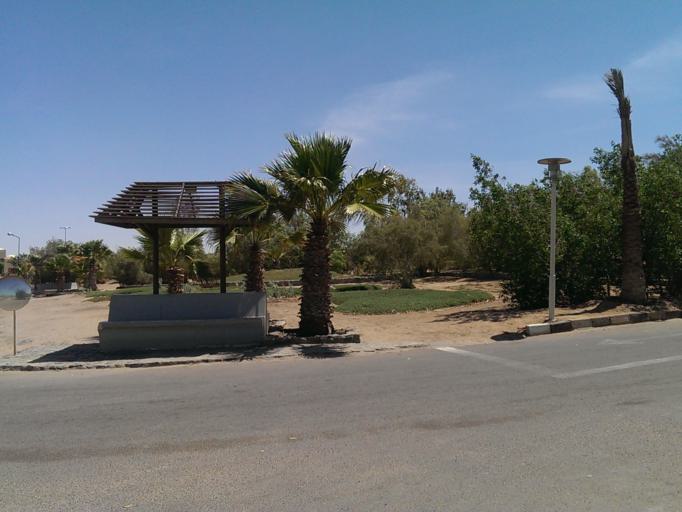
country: EG
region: Red Sea
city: El Gouna
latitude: 27.3961
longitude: 33.6710
